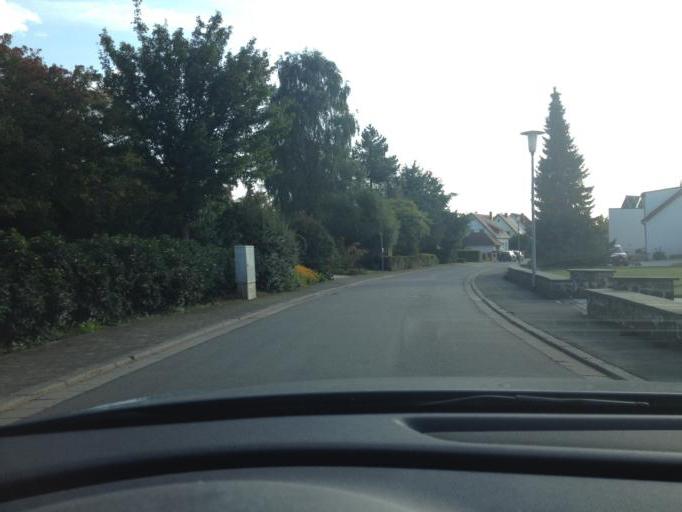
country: DE
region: Saarland
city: Sankt Wendel
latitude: 49.4575
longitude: 7.1730
